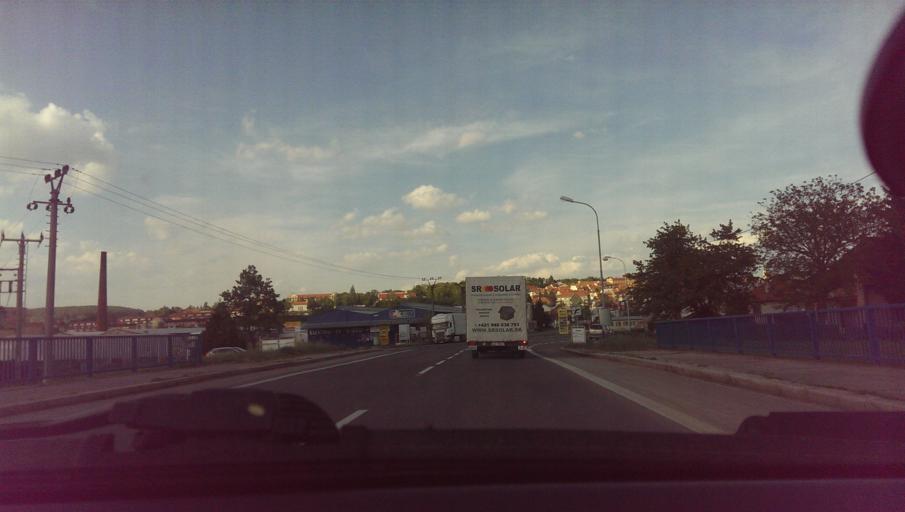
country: CZ
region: Zlin
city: Uhersky Brod
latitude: 49.0191
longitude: 17.6374
